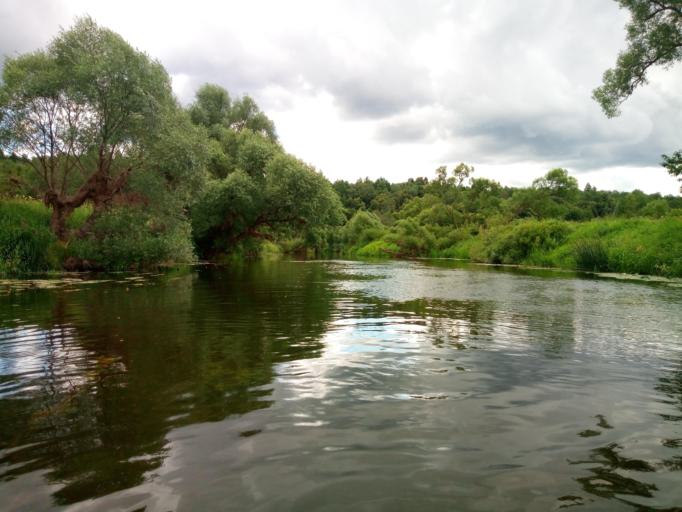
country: RU
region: Kaluga
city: Borovsk
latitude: 55.2071
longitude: 36.3573
